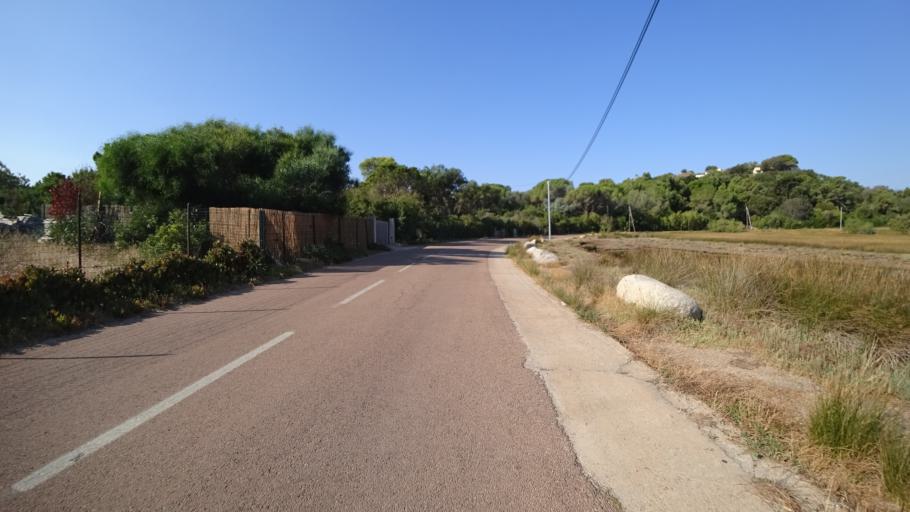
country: FR
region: Corsica
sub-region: Departement de la Corse-du-Sud
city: Porto-Vecchio
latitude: 41.6180
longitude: 9.3290
